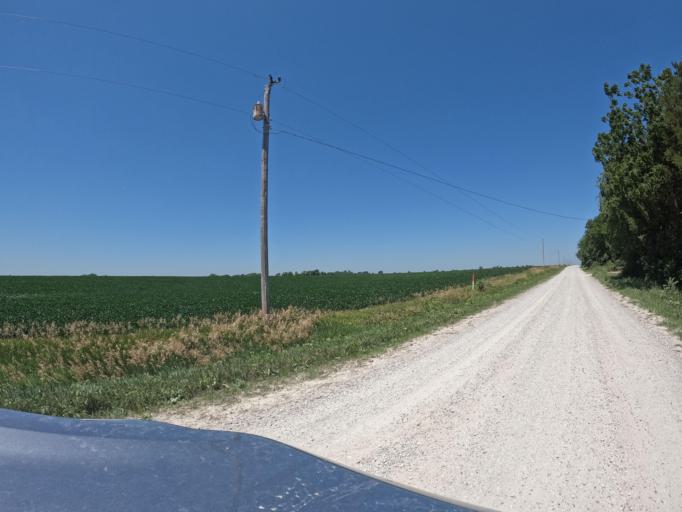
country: US
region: Iowa
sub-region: Keokuk County
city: Sigourney
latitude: 41.4602
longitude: -92.3358
